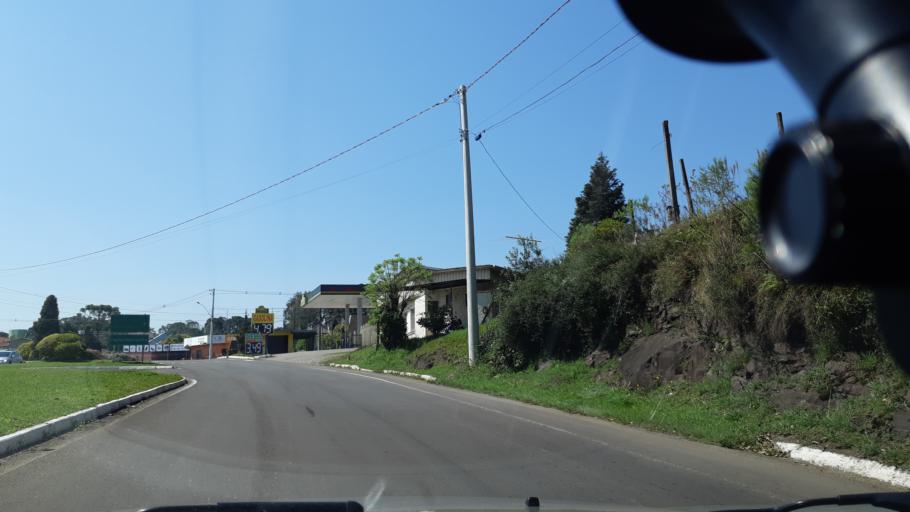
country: BR
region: Rio Grande do Sul
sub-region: Nova Petropolis
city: Nova Petropolis
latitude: -29.3869
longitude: -51.1254
